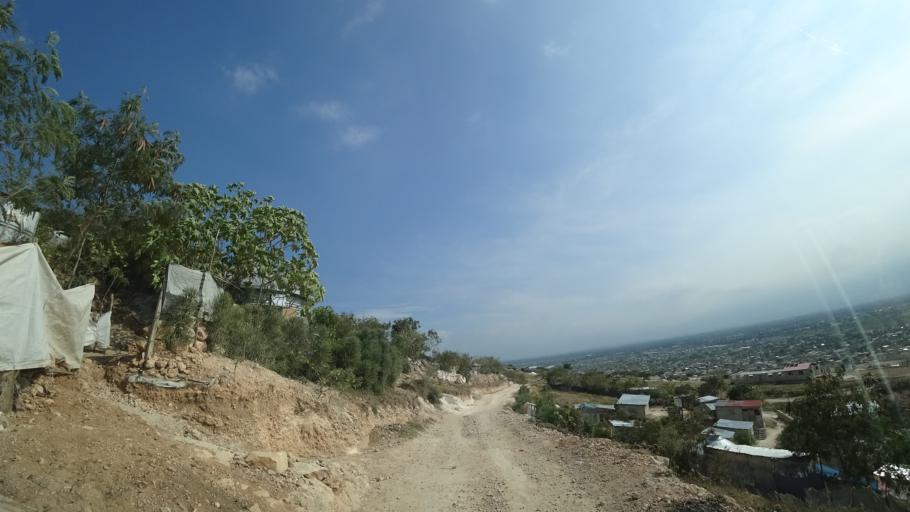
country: HT
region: Ouest
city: Croix des Bouquets
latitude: 18.6615
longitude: -72.2816
